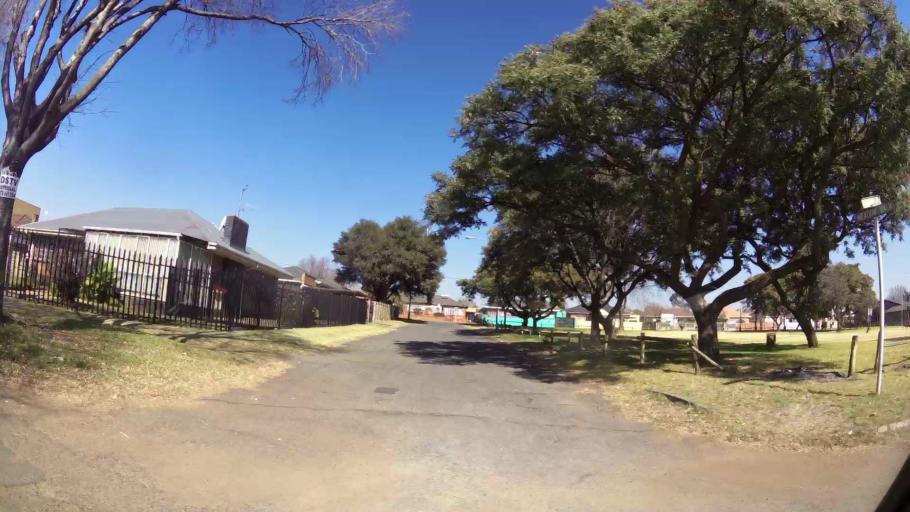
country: ZA
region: Gauteng
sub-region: City of Johannesburg Metropolitan Municipality
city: Johannesburg
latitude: -26.2419
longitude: 28.0751
